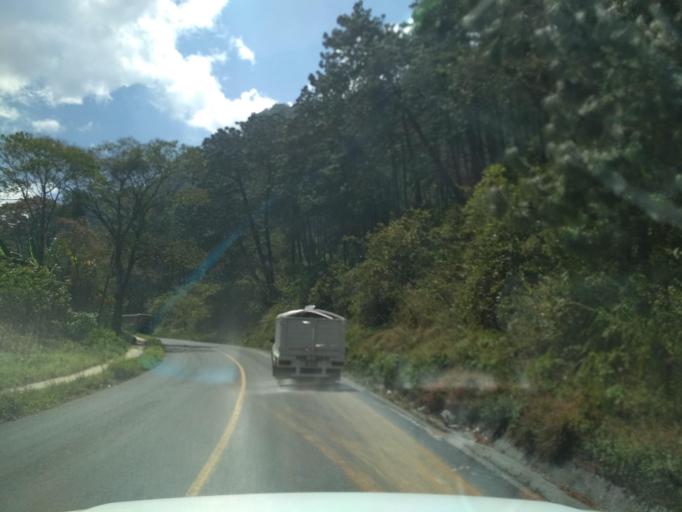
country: MX
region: Veracruz
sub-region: Tlilapan
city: Tonalixco
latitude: 18.7813
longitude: -97.0835
